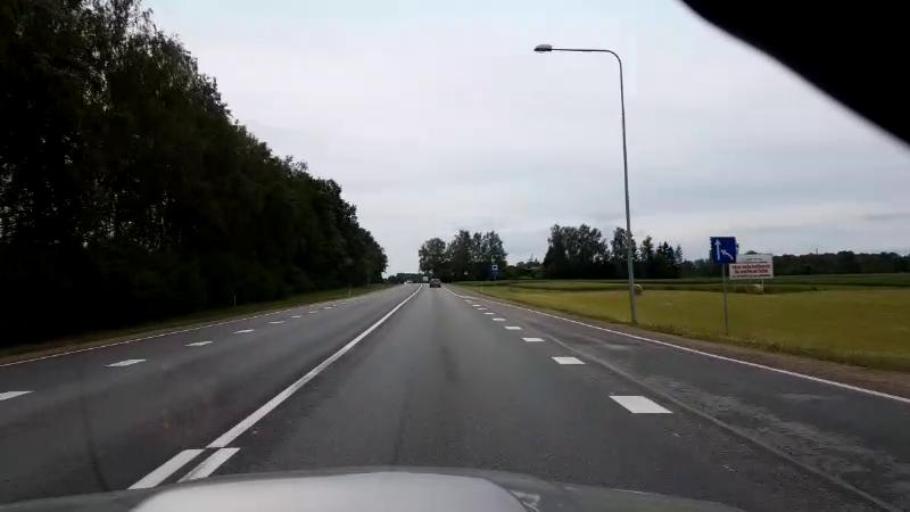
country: LV
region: Bauskas Rajons
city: Bauska
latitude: 56.4625
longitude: 24.1625
